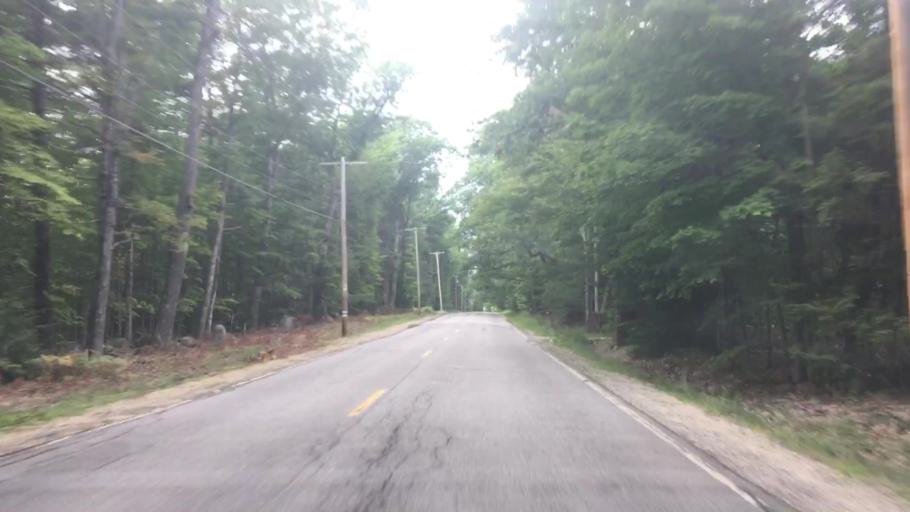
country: US
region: Maine
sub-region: Oxford County
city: Oxford
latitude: 44.0380
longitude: -70.5380
